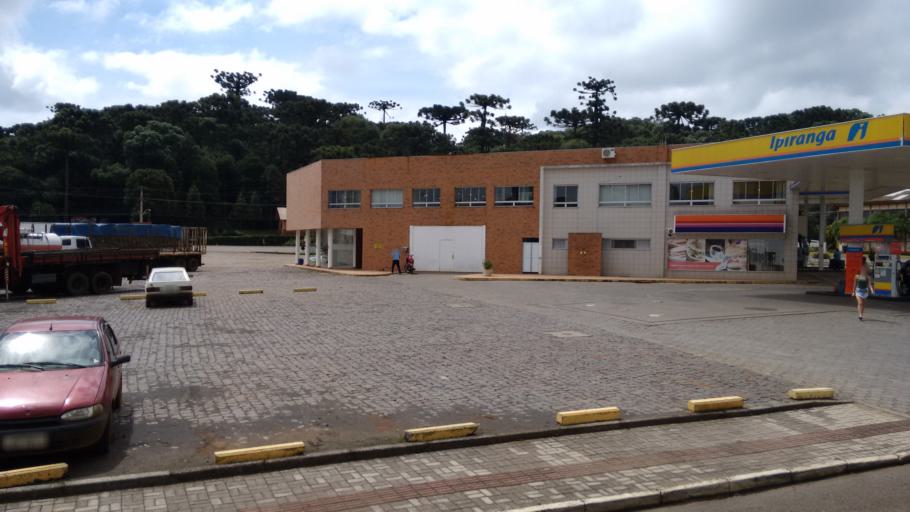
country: BR
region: Santa Catarina
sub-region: Videira
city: Videira
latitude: -27.0214
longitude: -50.9242
